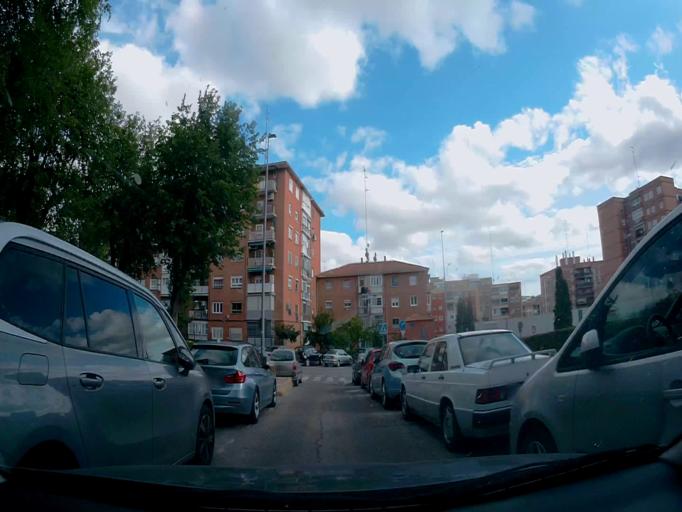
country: ES
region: Madrid
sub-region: Provincia de Madrid
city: Mostoles
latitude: 40.3206
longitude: -3.8733
